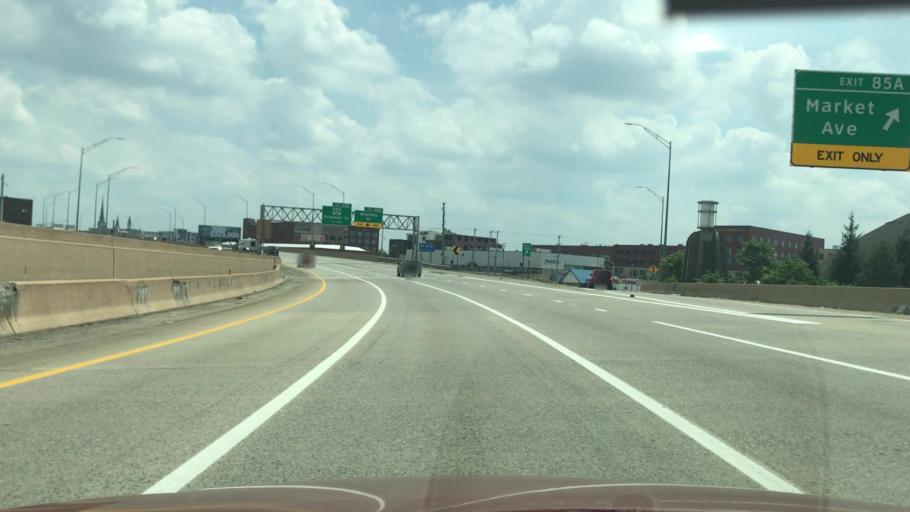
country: US
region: Michigan
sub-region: Kent County
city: Grand Rapids
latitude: 42.9616
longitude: -85.6775
